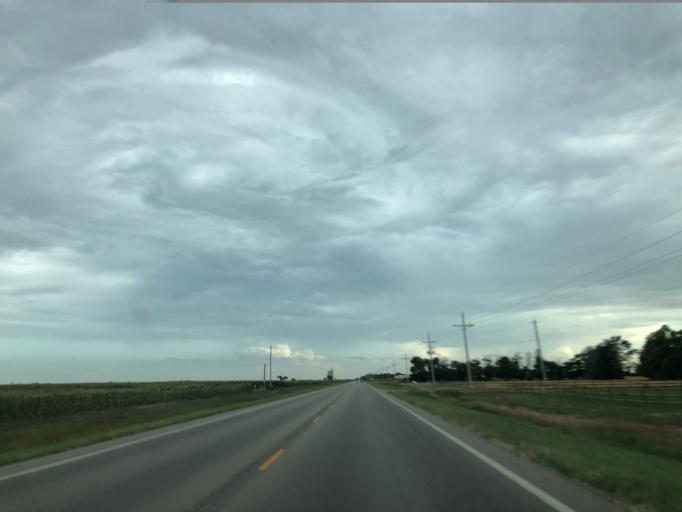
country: US
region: Kansas
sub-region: Rice County
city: Lyons
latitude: 38.2886
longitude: -98.2020
